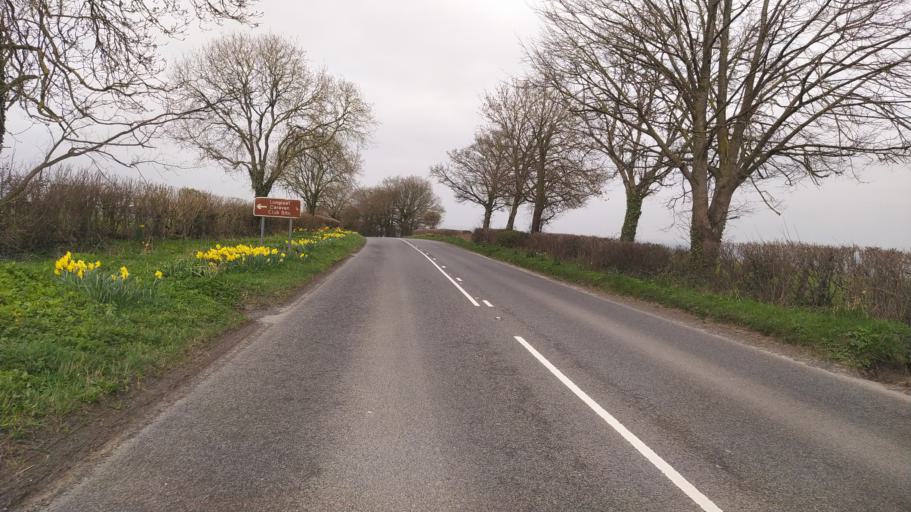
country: GB
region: England
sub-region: Wiltshire
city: Corsley
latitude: 51.2100
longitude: -2.2653
